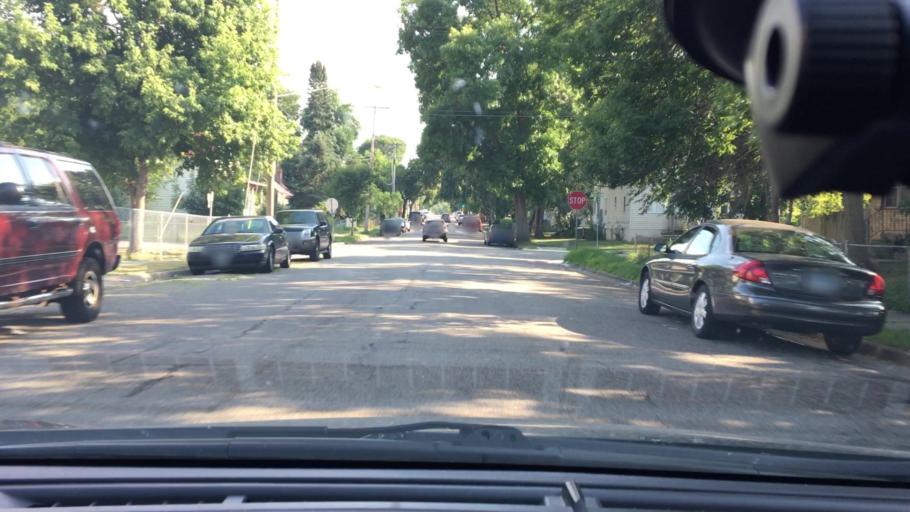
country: US
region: Minnesota
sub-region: Hennepin County
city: Minneapolis
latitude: 44.9830
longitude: -93.3046
